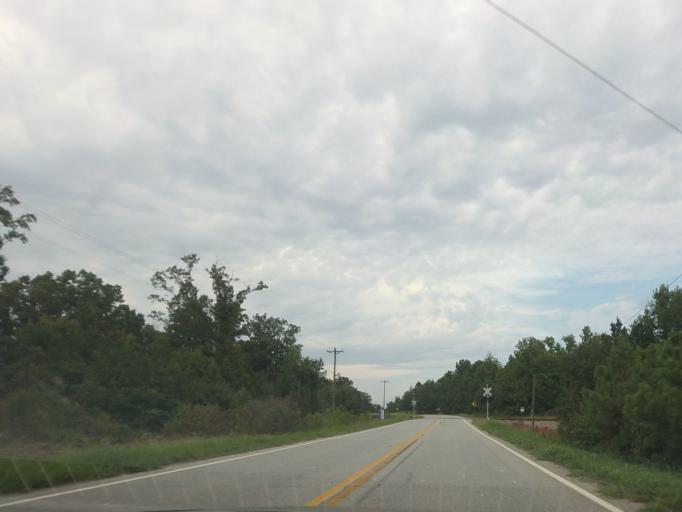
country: US
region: Georgia
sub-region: Twiggs County
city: Jeffersonville
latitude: 32.7572
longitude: -83.4439
